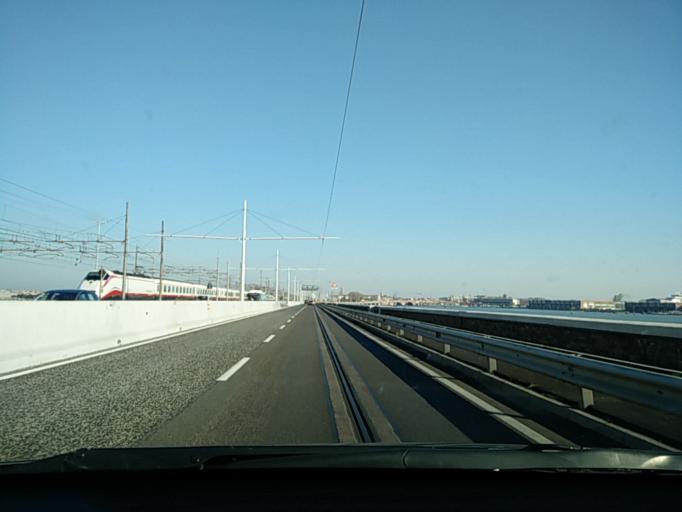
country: IT
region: Veneto
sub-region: Provincia di Venezia
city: Venice
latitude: 45.4501
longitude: 12.3050
